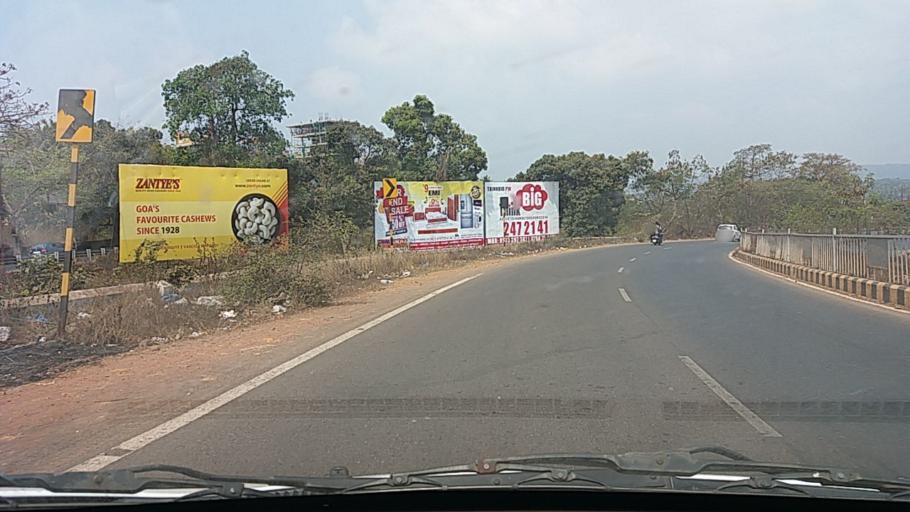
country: IN
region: Goa
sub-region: North Goa
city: Bambolim
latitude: 15.4647
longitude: 73.8528
